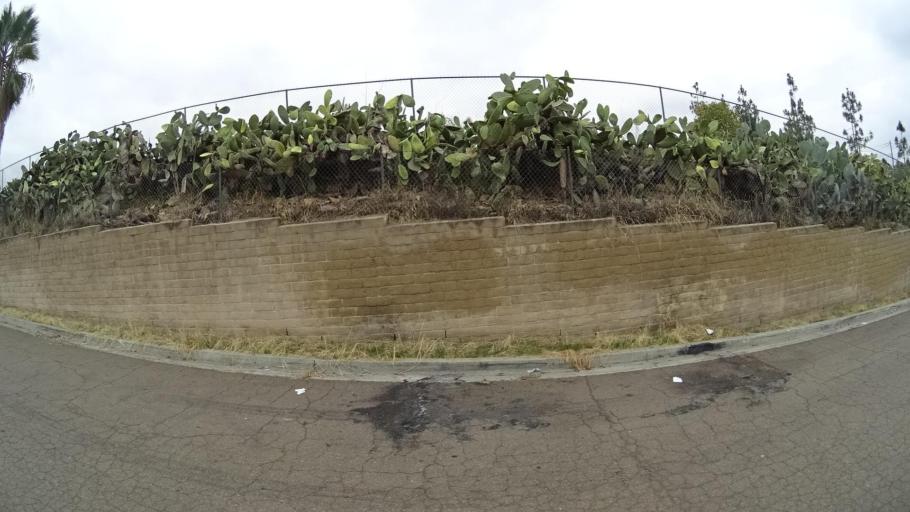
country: US
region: California
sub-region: San Diego County
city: Spring Valley
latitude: 32.7385
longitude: -117.0024
